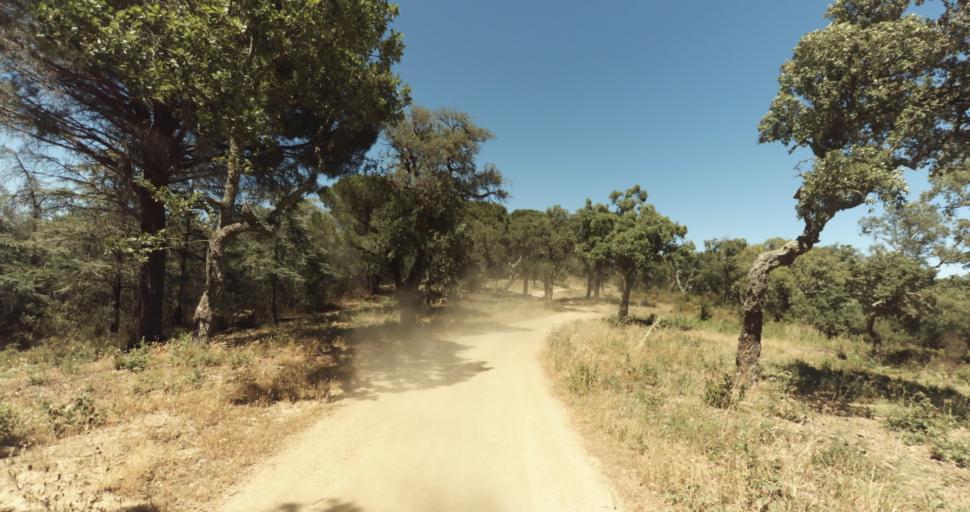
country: FR
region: Provence-Alpes-Cote d'Azur
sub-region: Departement du Var
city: Gassin
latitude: 43.2486
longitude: 6.5621
